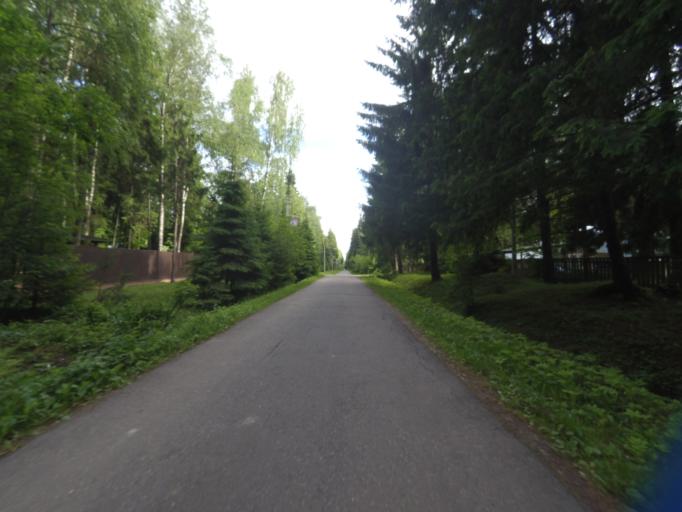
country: RU
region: Moskovskaya
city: Nekrasovskiy
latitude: 56.1160
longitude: 37.5172
